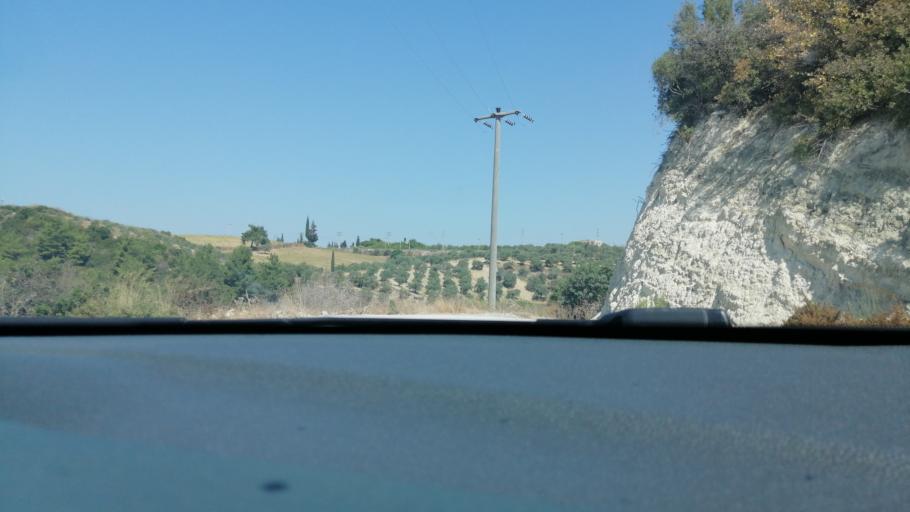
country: TR
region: Aydin
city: Davutlar
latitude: 37.7826
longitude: 27.3141
